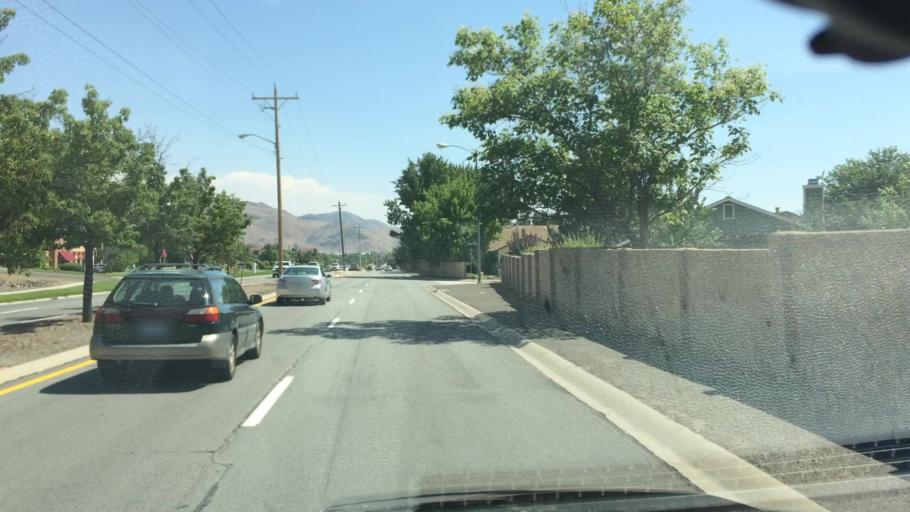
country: US
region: Nevada
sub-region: Washoe County
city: Sparks
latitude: 39.5619
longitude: -119.7056
